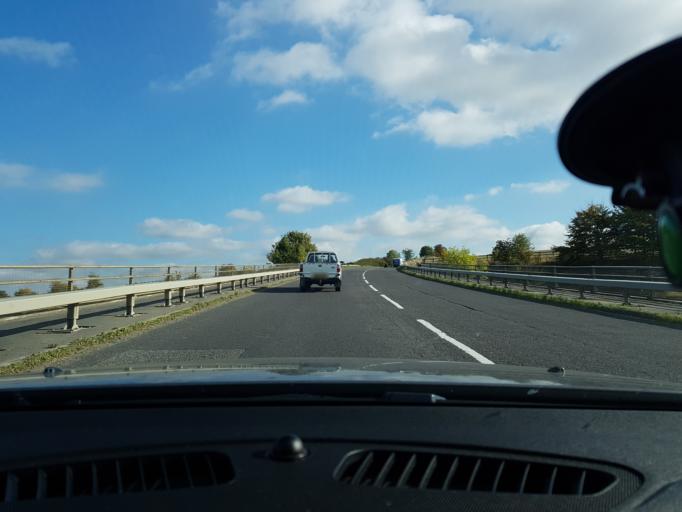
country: GB
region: England
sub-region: Borough of Swindon
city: Wanborough
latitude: 51.5271
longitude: -1.6918
